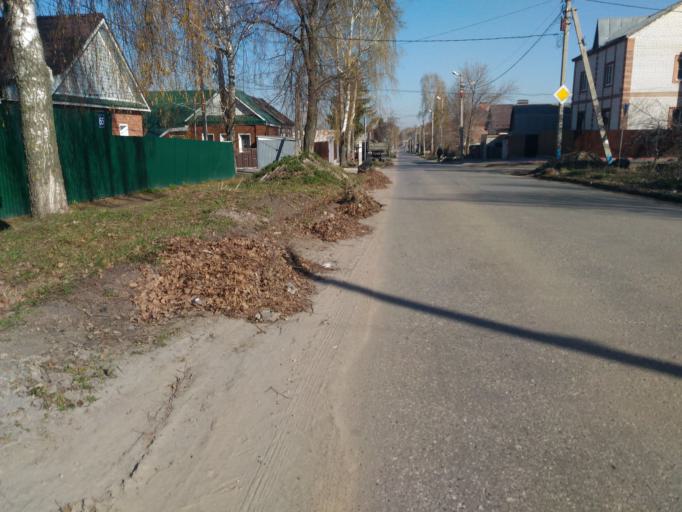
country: RU
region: Ulyanovsk
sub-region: Ulyanovskiy Rayon
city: Ulyanovsk
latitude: 54.3496
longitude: 48.3776
